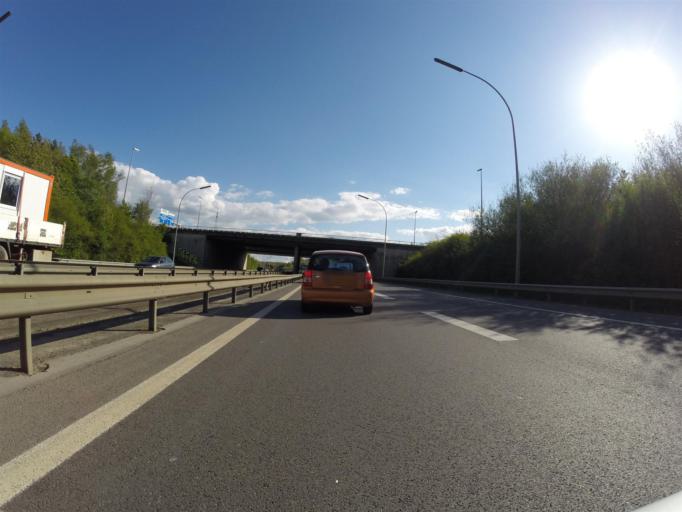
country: LU
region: Luxembourg
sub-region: Canton de Luxembourg
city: Hesperange
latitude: 49.5774
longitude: 6.1249
